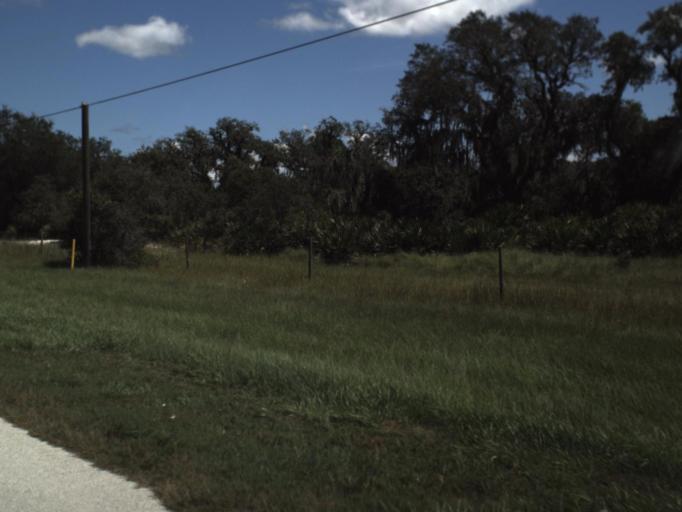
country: US
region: Florida
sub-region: Polk County
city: Frostproof
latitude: 27.6858
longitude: -81.5473
